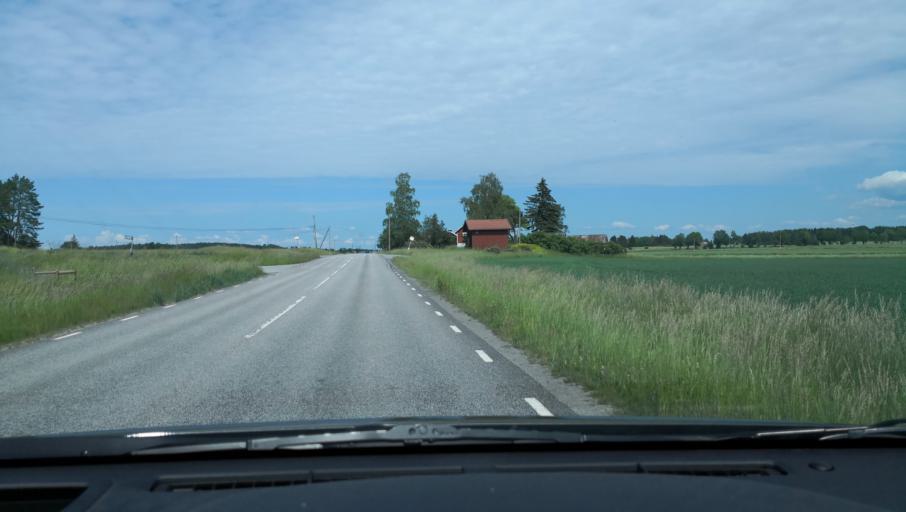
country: SE
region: Stockholm
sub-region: Sigtuna Kommun
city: Sigtuna
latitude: 59.6639
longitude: 17.6907
